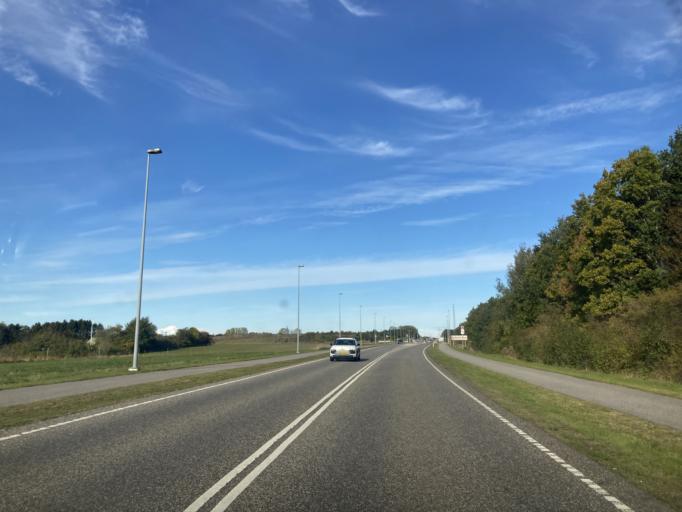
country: DK
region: Capital Region
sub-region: Vallensbaek Kommune
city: Vallensbaek
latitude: 55.6363
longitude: 12.3743
